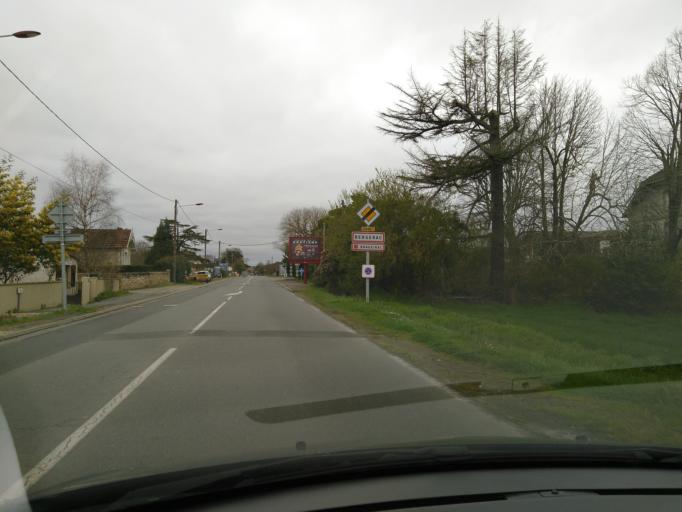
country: FR
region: Aquitaine
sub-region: Departement de la Dordogne
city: Bergerac
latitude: 44.8385
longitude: 0.4894
